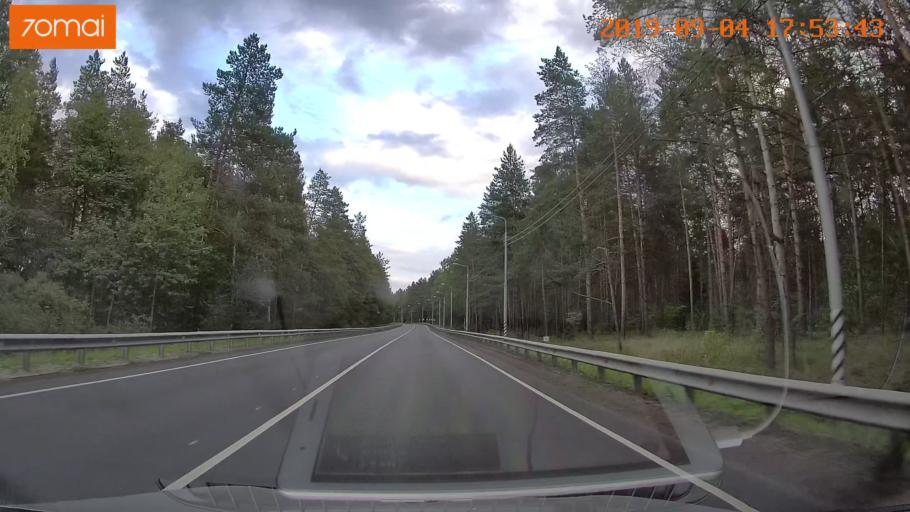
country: RU
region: Moskovskaya
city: Imeni Tsyurupy
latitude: 55.5147
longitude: 38.7273
